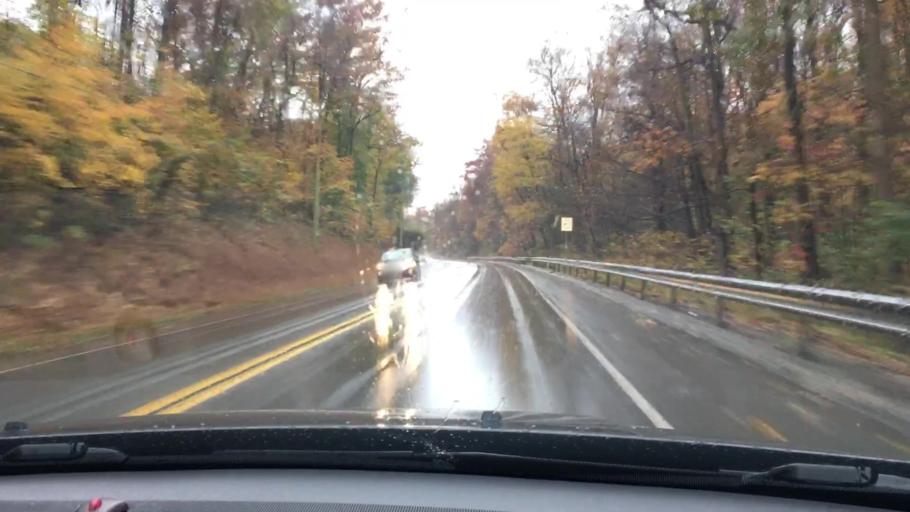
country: US
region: Pennsylvania
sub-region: York County
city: Susquehanna Trails
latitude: 39.8071
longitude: -76.3393
